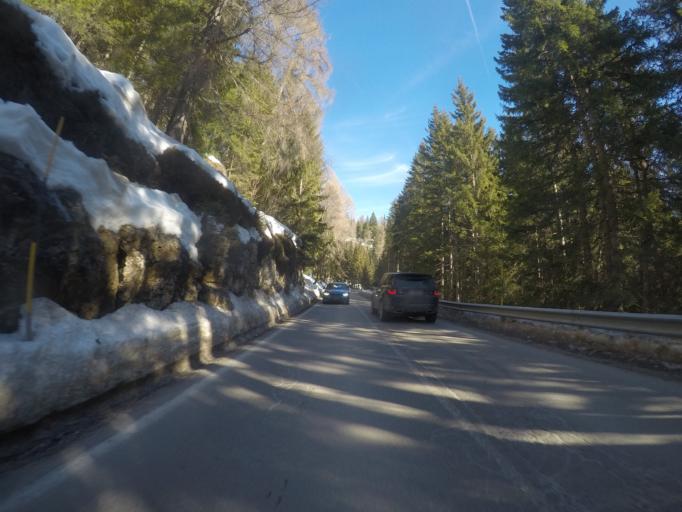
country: IT
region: Veneto
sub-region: Provincia di Belluno
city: Cortina d'Ampezzo
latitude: 46.5220
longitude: 12.1157
